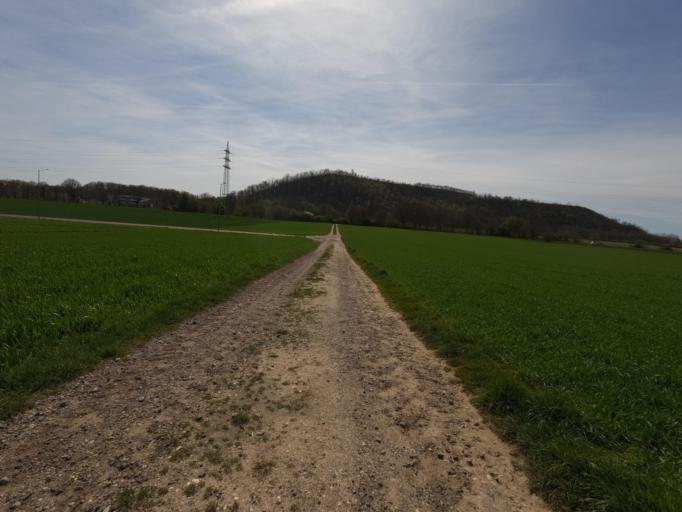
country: DE
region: North Rhine-Westphalia
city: Baesweiler
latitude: 50.9161
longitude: 6.1630
